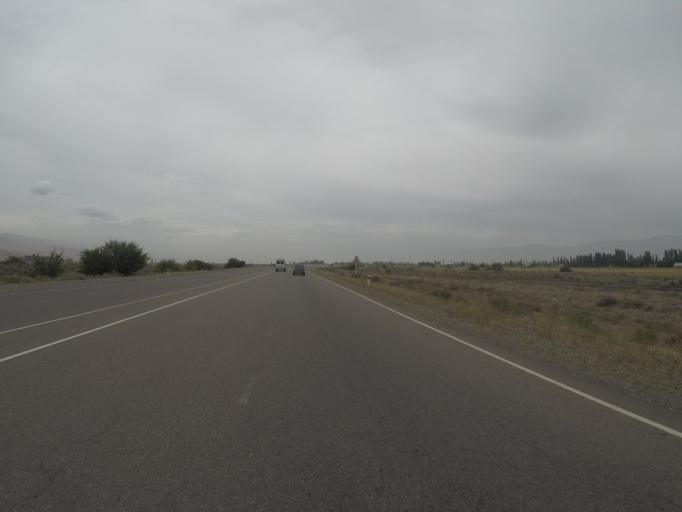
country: KG
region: Chuy
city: Bystrovka
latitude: 42.8285
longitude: 75.5359
